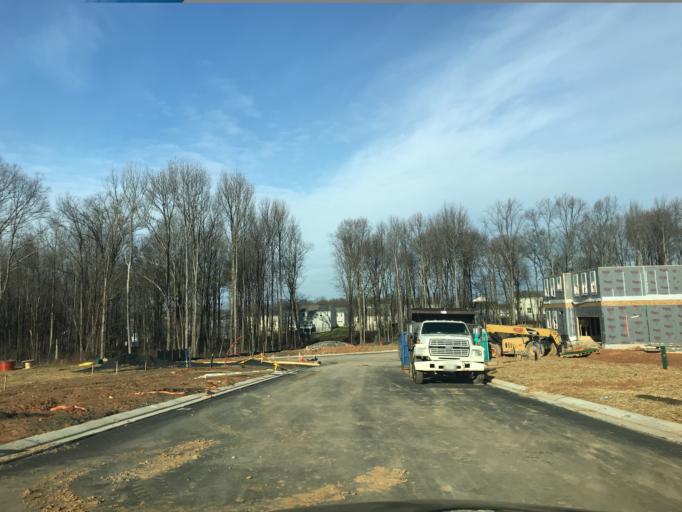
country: US
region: Maryland
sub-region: Baltimore County
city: Middle River
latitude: 39.3579
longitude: -76.4319
